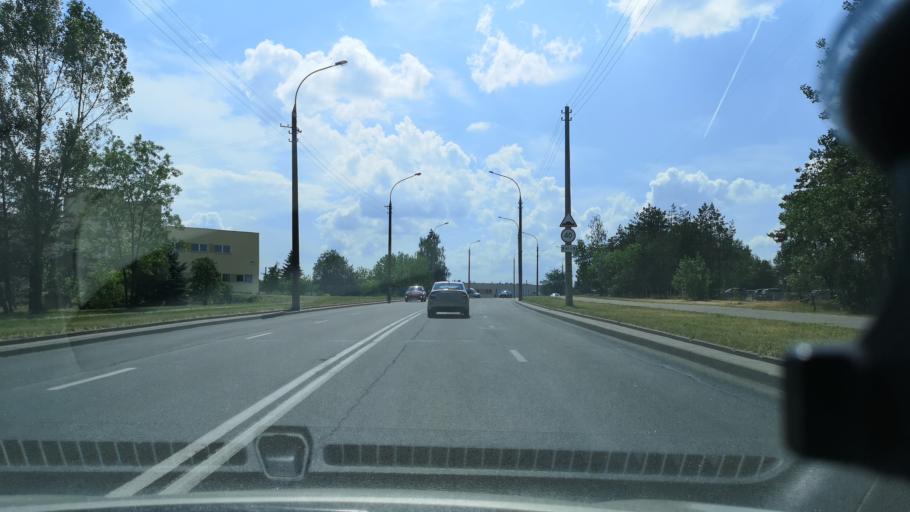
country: BY
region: Minsk
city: Vyaliki Trastsyanets
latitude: 53.9262
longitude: 27.6982
